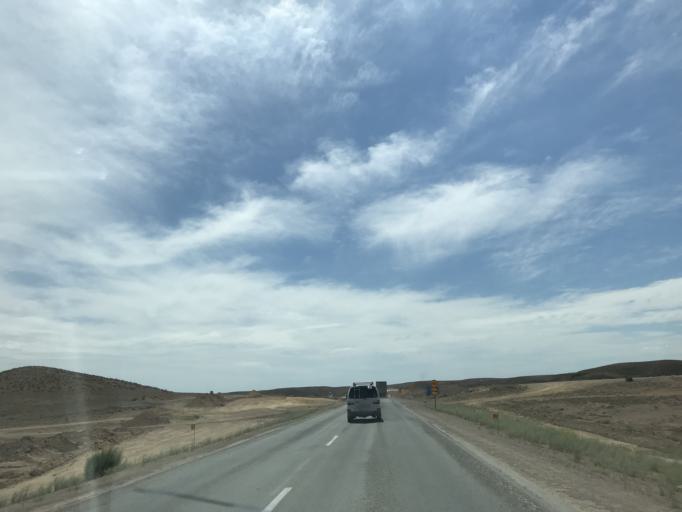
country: KZ
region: Almaty Oblysy
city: Ulken
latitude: 45.0699
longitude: 73.9925
